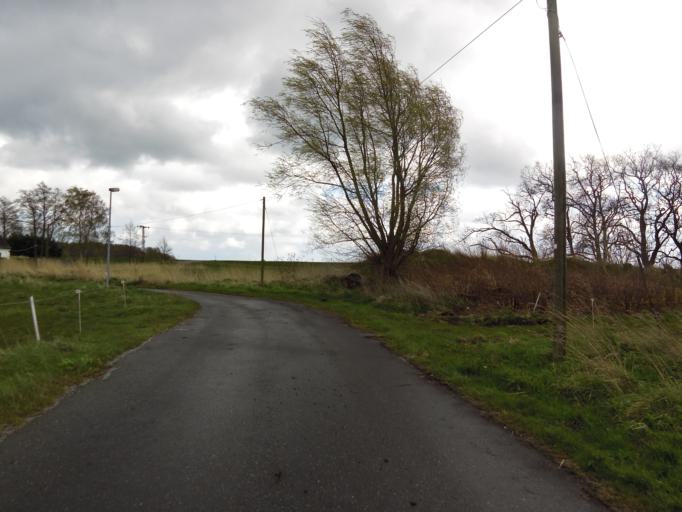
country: DE
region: Mecklenburg-Vorpommern
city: Barth
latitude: 54.4201
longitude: 12.7964
